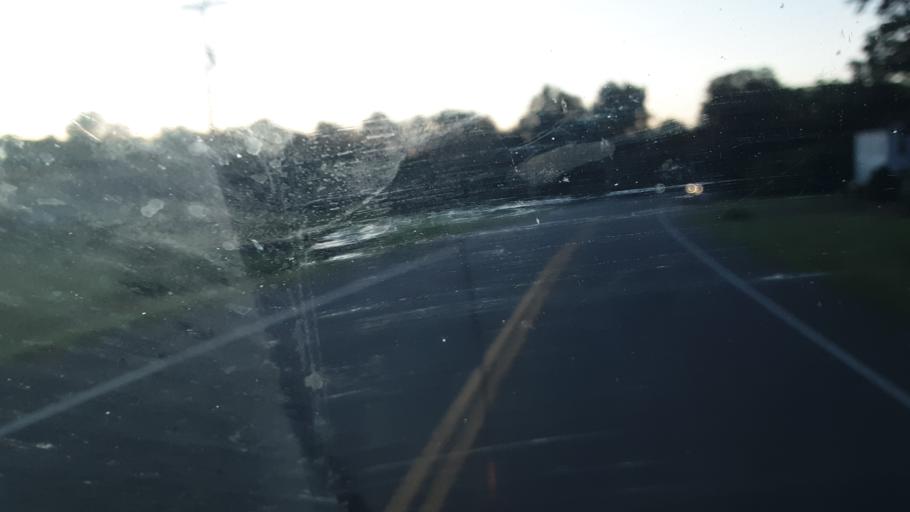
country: US
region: New York
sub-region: Montgomery County
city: Hagaman
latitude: 42.9761
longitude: -74.0619
